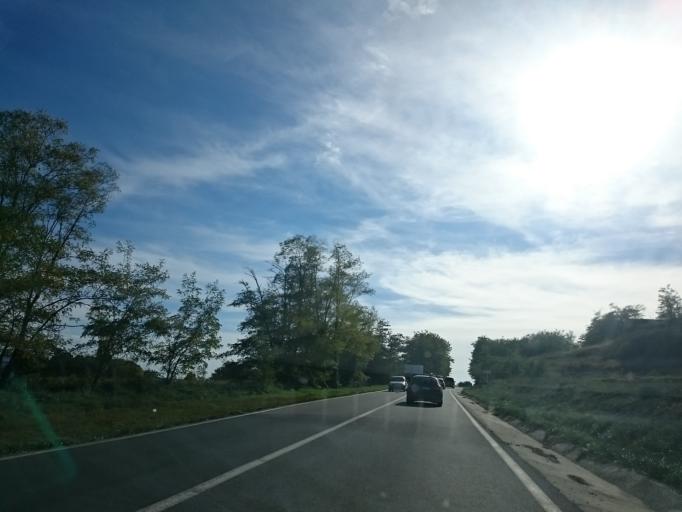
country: ES
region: Catalonia
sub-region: Provincia de Barcelona
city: Vic
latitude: 41.9486
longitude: 2.2744
